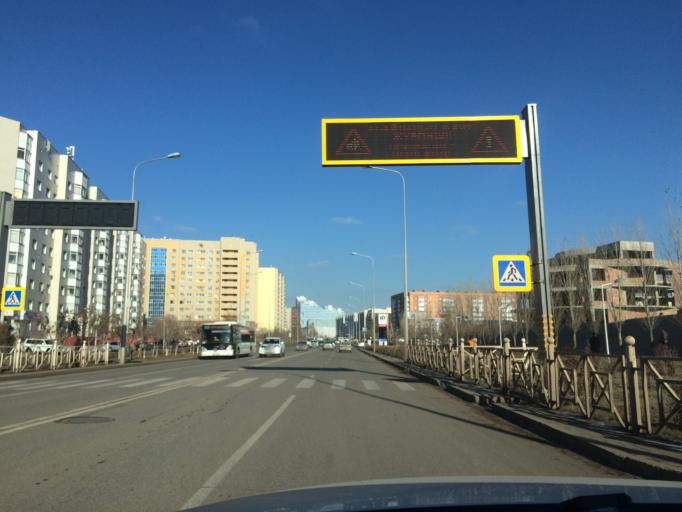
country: KZ
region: Astana Qalasy
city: Astana
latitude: 51.1195
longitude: 71.4199
